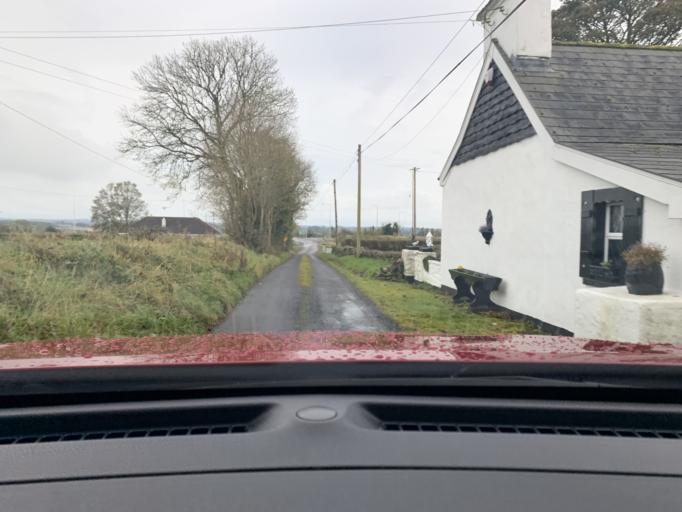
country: IE
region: Connaught
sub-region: Roscommon
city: Ballaghaderreen
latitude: 53.9145
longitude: -8.5545
